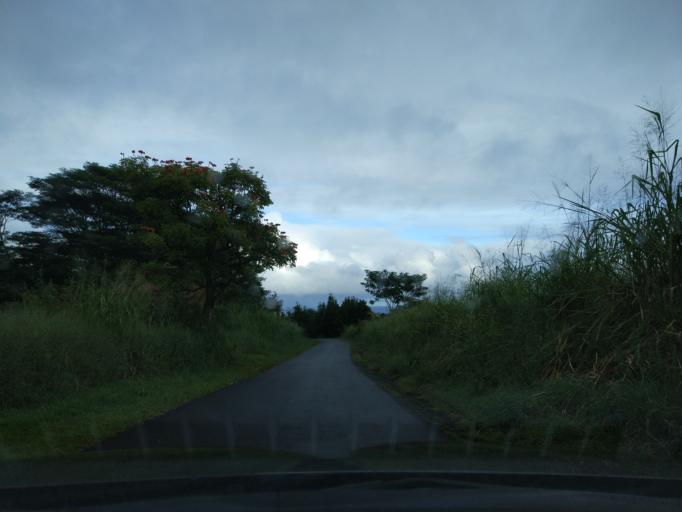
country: US
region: Hawaii
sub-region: Hawaii County
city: Pepeekeo
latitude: 19.8730
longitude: -155.1343
